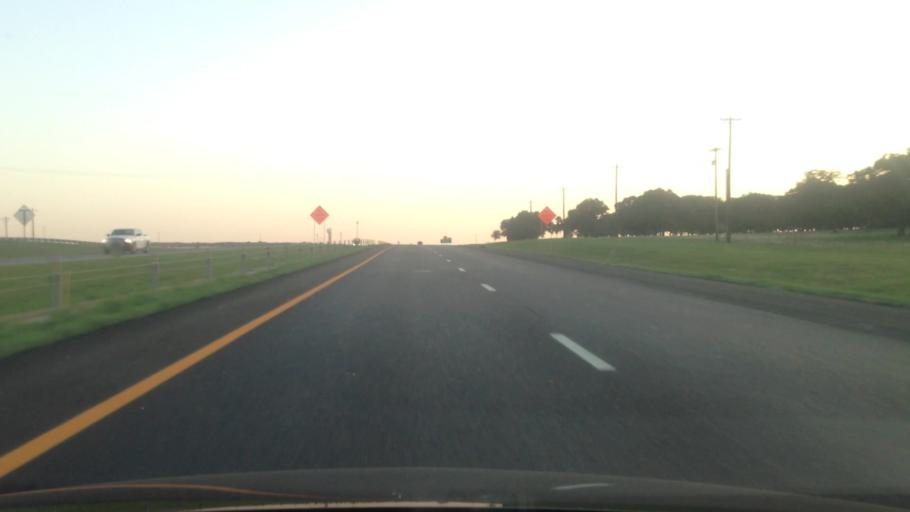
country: US
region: Texas
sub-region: Denton County
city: Argyle
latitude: 33.1511
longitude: -97.1939
